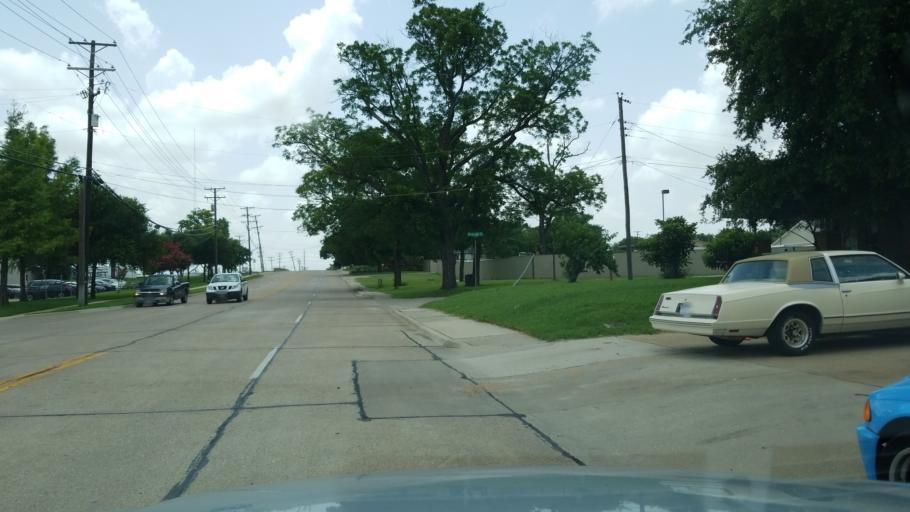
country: US
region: Texas
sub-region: Dallas County
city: Irving
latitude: 32.8236
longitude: -96.9074
